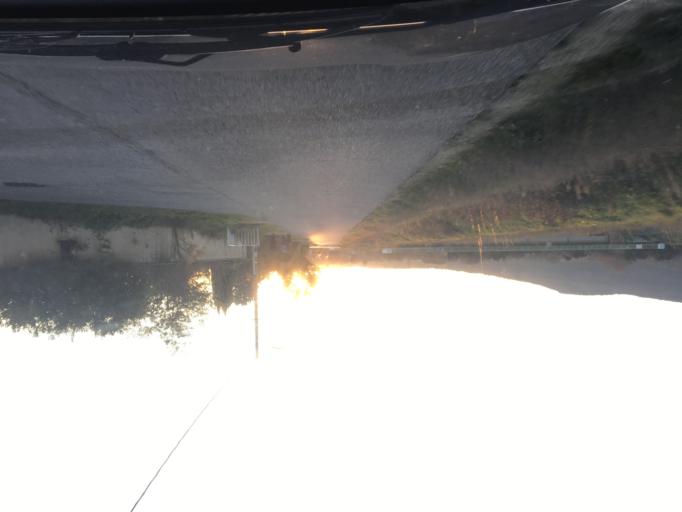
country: FR
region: Provence-Alpes-Cote d'Azur
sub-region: Departement des Bouches-du-Rhone
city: Mallemort
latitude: 43.7229
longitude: 5.1833
